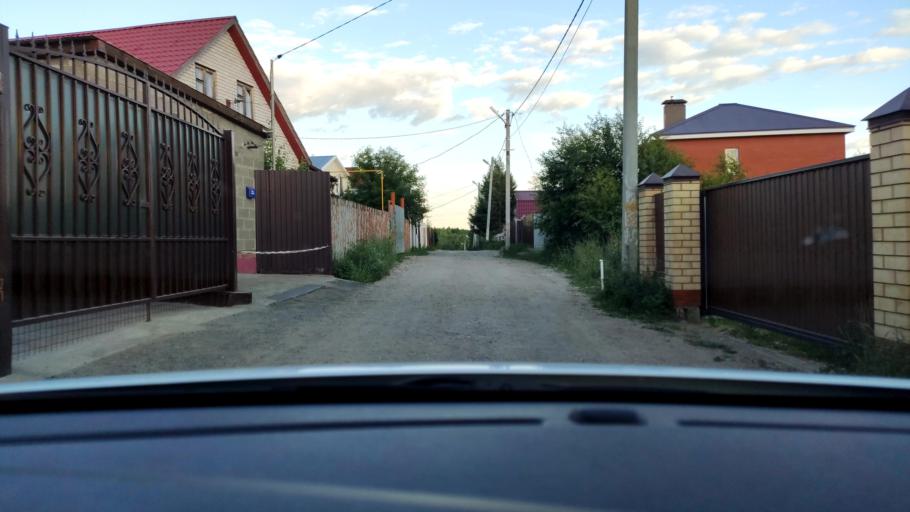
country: RU
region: Tatarstan
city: Stolbishchi
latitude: 55.7604
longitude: 49.3021
